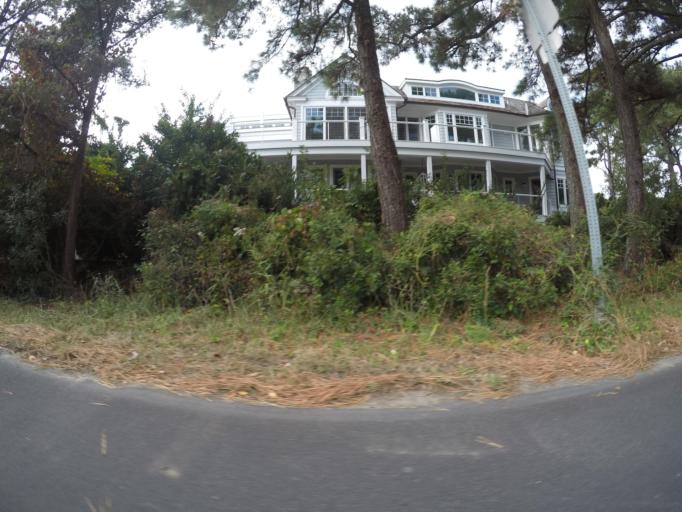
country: US
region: Delaware
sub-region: Sussex County
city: Rehoboth Beach
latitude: 38.7281
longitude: -75.0796
